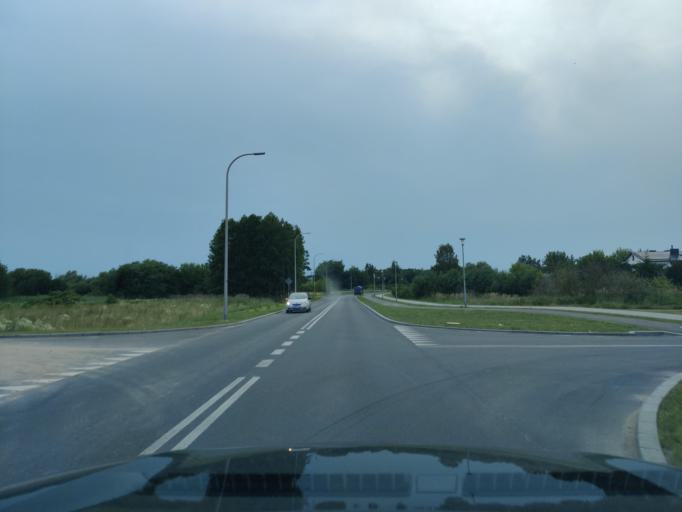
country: PL
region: Masovian Voivodeship
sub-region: Powiat mlawski
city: Mlawa
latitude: 53.1035
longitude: 20.3708
